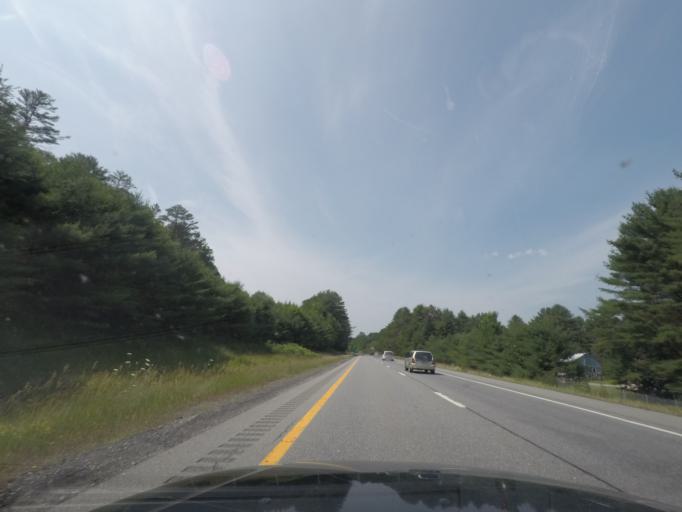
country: US
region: New York
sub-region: Warren County
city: Warrensburg
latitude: 43.6613
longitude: -73.7688
